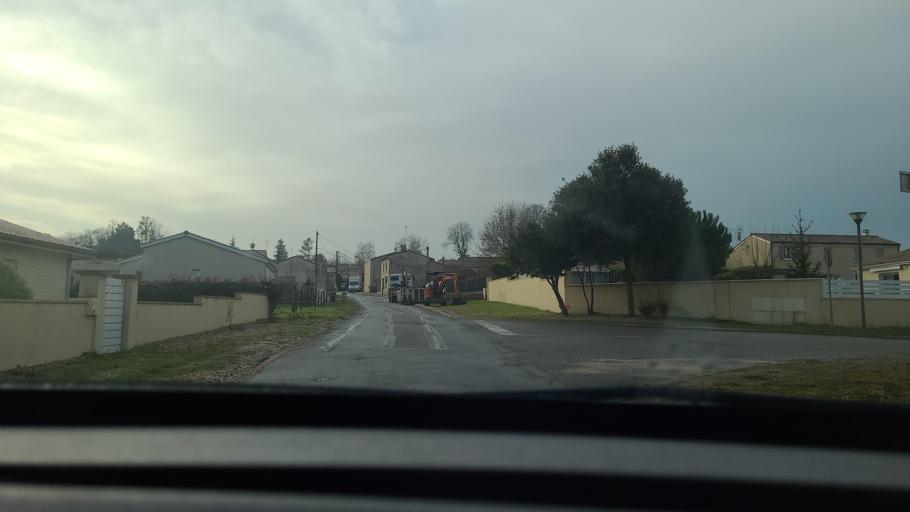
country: FR
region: Aquitaine
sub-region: Departement de la Gironde
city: Marcamps
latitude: 45.0375
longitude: -0.4696
